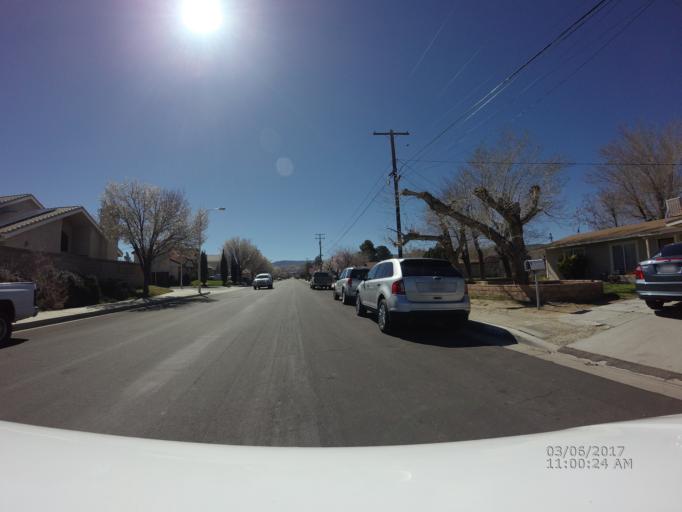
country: US
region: California
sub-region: Los Angeles County
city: Quartz Hill
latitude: 34.6561
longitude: -118.2232
